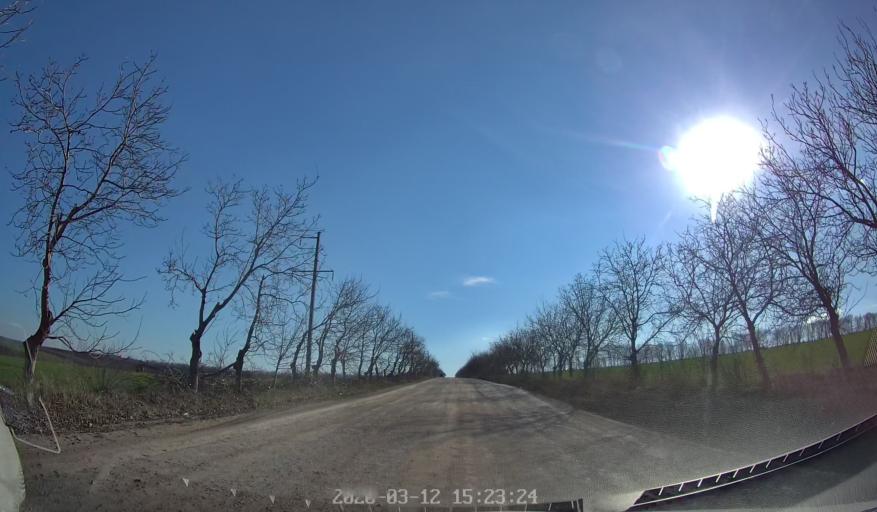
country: MD
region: Chisinau
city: Ciorescu
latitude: 47.1922
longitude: 28.9166
